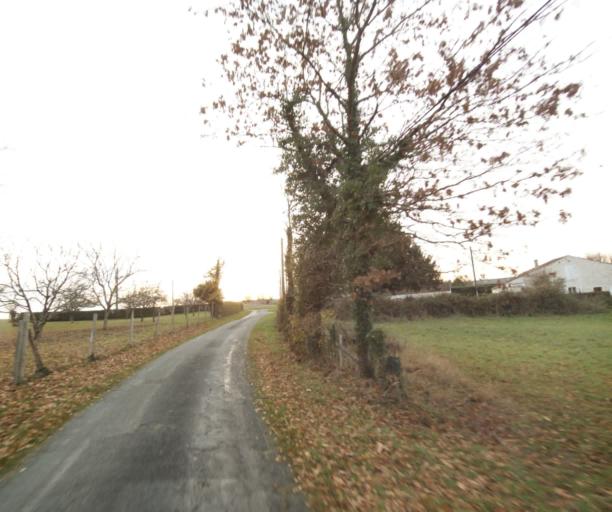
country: FR
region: Poitou-Charentes
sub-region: Departement de la Charente-Maritime
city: Bussac-sur-Charente
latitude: 45.8092
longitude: -0.6051
